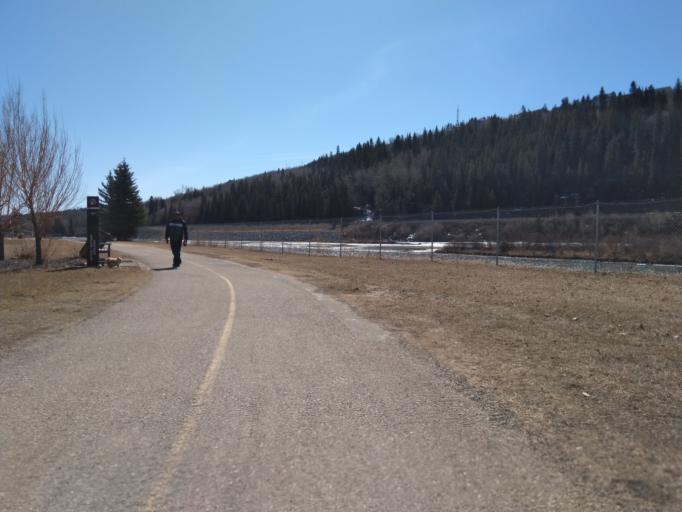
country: CA
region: Alberta
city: Calgary
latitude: 51.0710
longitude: -114.1717
